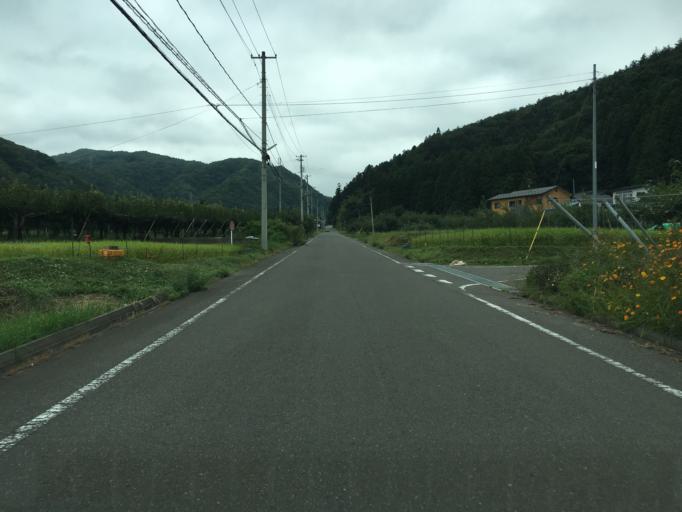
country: JP
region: Fukushima
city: Fukushima-shi
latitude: 37.7946
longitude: 140.3864
